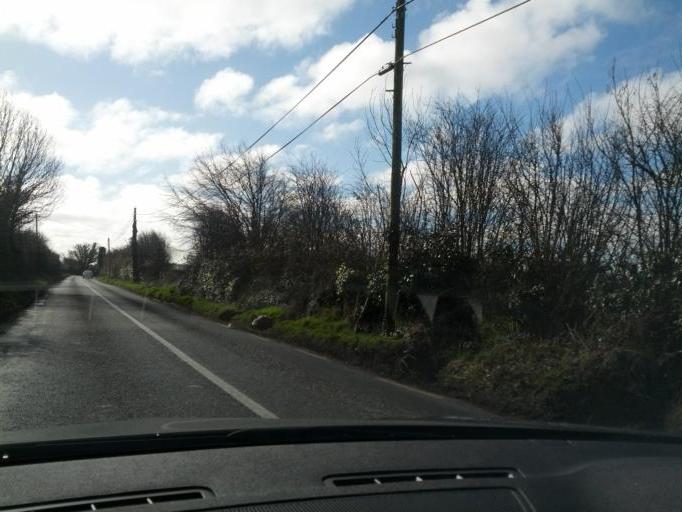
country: IE
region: Connaught
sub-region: County Galway
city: Ballinasloe
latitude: 53.4063
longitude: -8.3357
